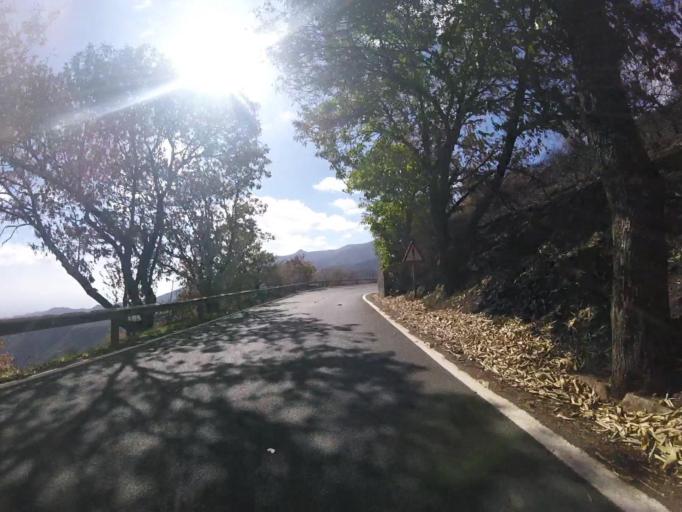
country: ES
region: Canary Islands
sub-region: Provincia de Las Palmas
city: Valleseco
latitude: 28.0103
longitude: -15.5842
